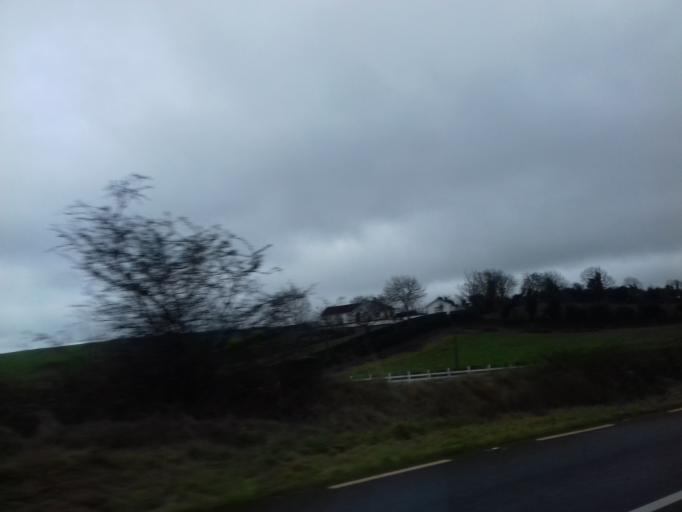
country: IE
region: Ulster
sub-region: County Monaghan
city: Castleblayney
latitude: 54.0788
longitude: -6.6811
